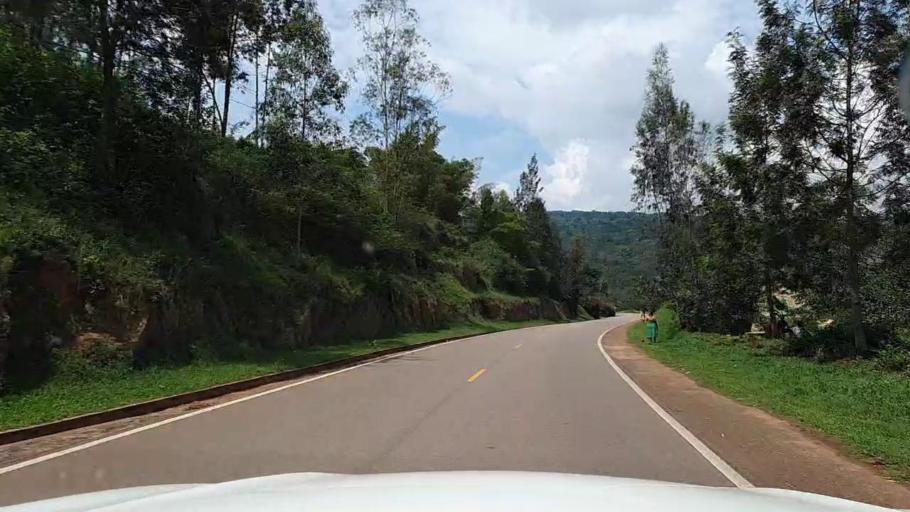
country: RW
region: Kigali
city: Kigali
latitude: -1.8434
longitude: 30.0911
